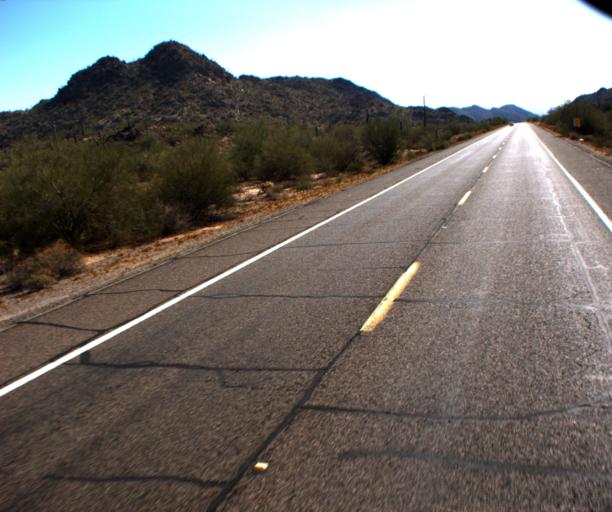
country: US
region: Arizona
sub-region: Pinal County
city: Sacaton
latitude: 33.0109
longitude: -111.6903
